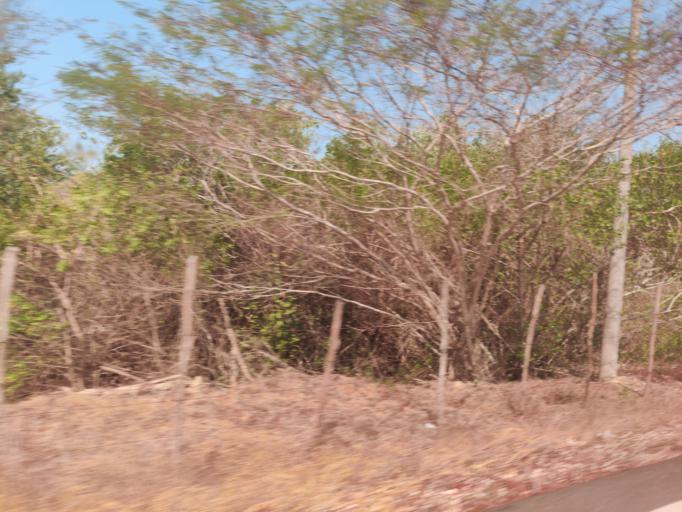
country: CO
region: Bolivar
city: Turbana
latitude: 10.1705
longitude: -75.6483
